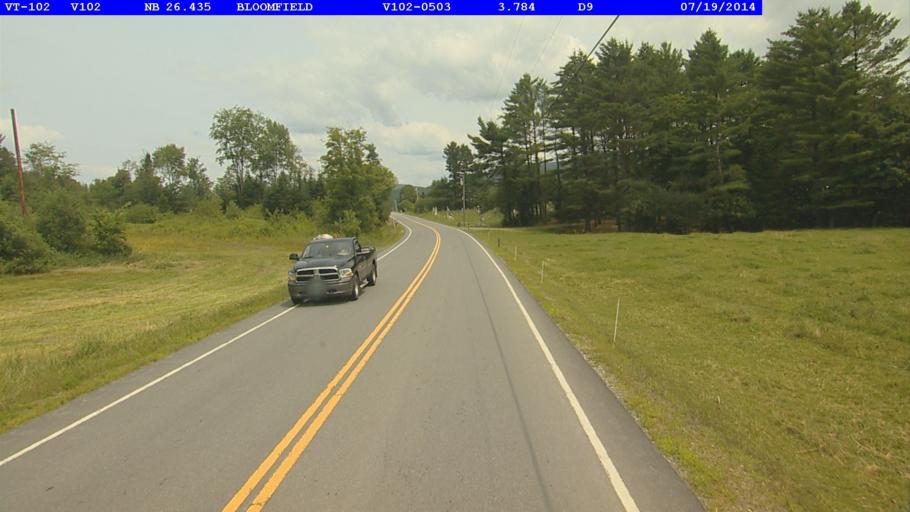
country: US
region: New Hampshire
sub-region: Coos County
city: Stratford
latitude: 44.7870
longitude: -71.5833
